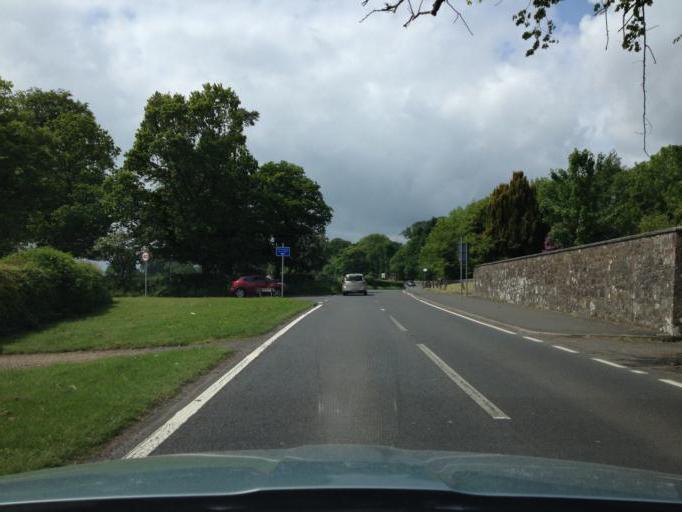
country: GB
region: Scotland
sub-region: Renfrewshire
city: Bishopton
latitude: 55.9154
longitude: -4.4861
